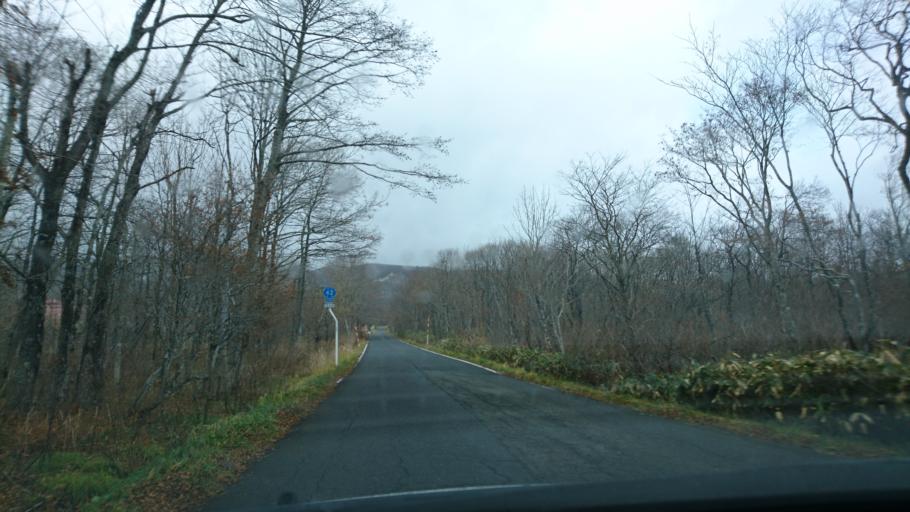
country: JP
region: Iwate
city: Ichinoseki
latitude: 38.9336
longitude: 140.8346
